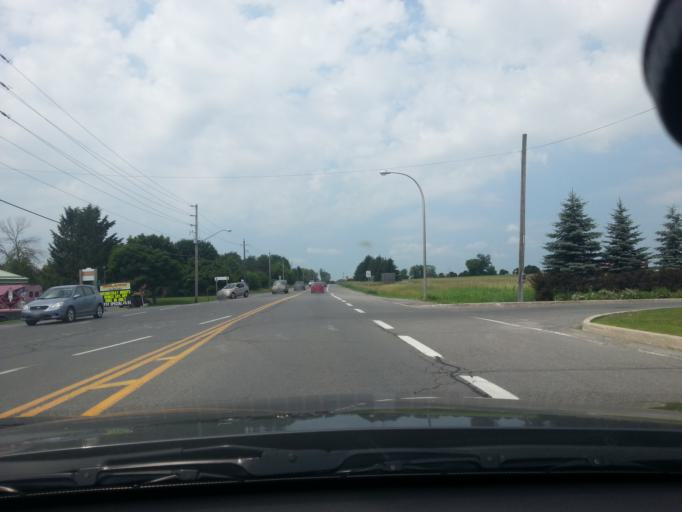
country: CA
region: Ontario
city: Bells Corners
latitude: 45.2342
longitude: -75.6767
